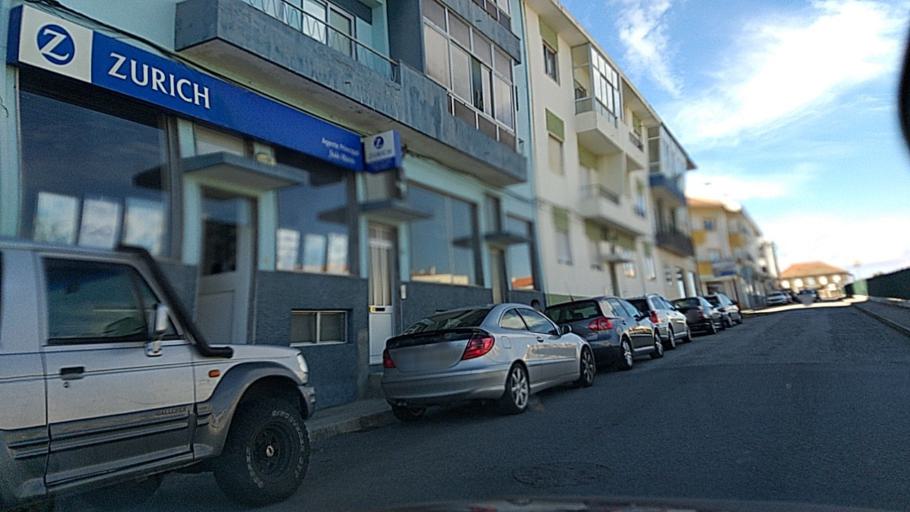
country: PT
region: Guarda
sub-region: Guarda
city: Sequeira
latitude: 40.5540
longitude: -7.2409
